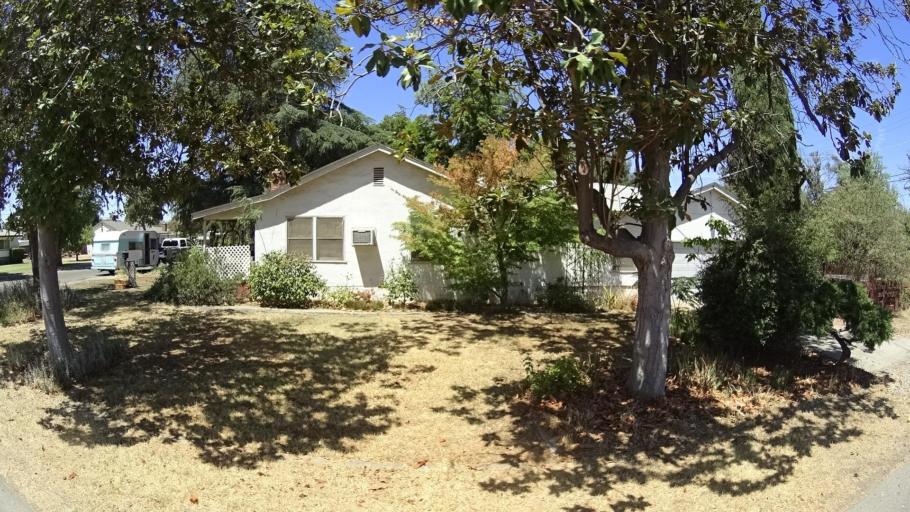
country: US
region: California
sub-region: Fresno County
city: Sunnyside
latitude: 36.7480
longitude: -119.7296
